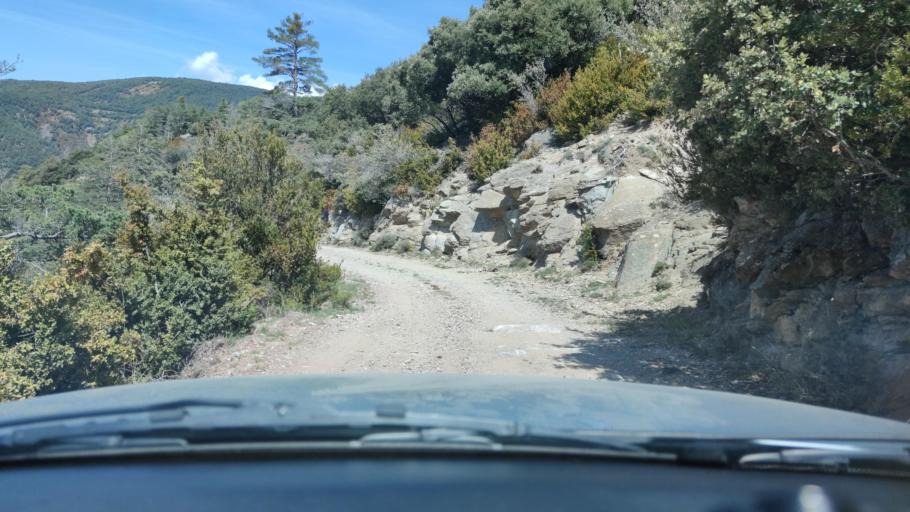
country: ES
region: Catalonia
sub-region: Provincia de Lleida
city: Sort
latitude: 42.3100
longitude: 1.1501
